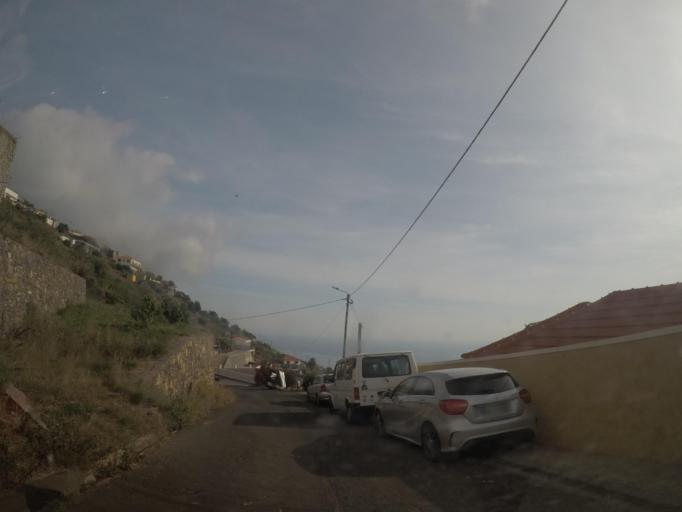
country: PT
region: Madeira
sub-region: Calheta
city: Faja da Ovelha
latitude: 32.7771
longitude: -17.2382
